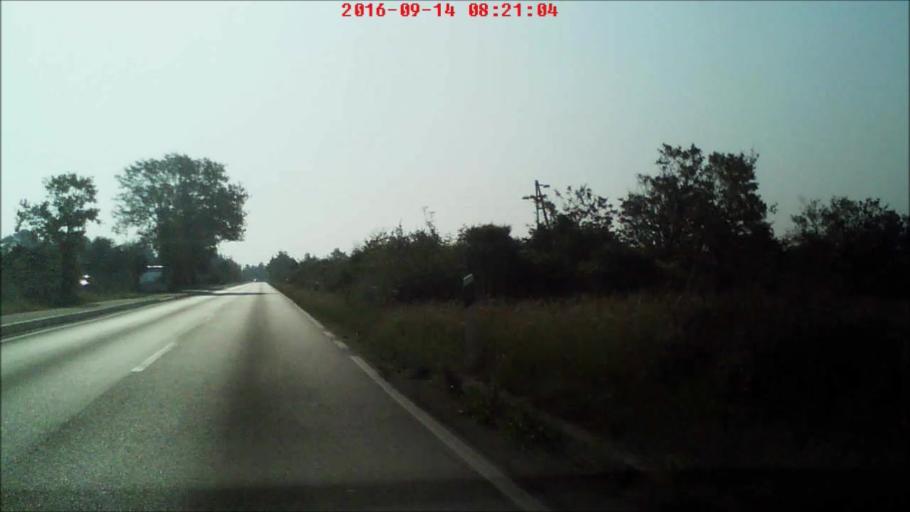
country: HR
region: Zadarska
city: Nin
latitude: 44.2240
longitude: 15.2073
